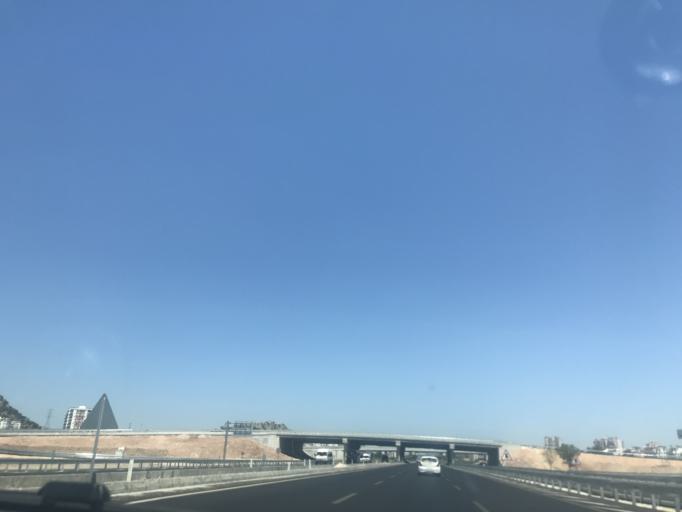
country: TR
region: Antalya
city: Cakirlar
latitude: 36.8453
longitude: 30.5998
